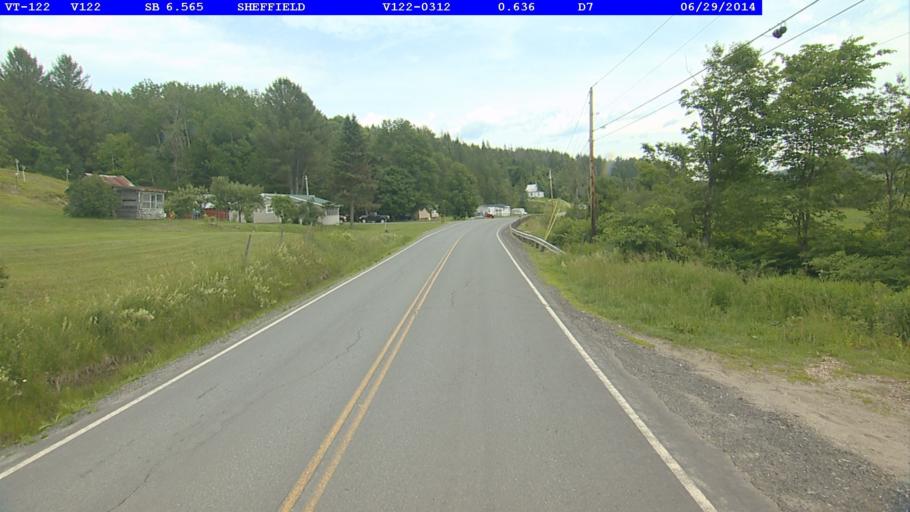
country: US
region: Vermont
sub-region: Caledonia County
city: Lyndonville
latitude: 44.5957
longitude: -72.1018
